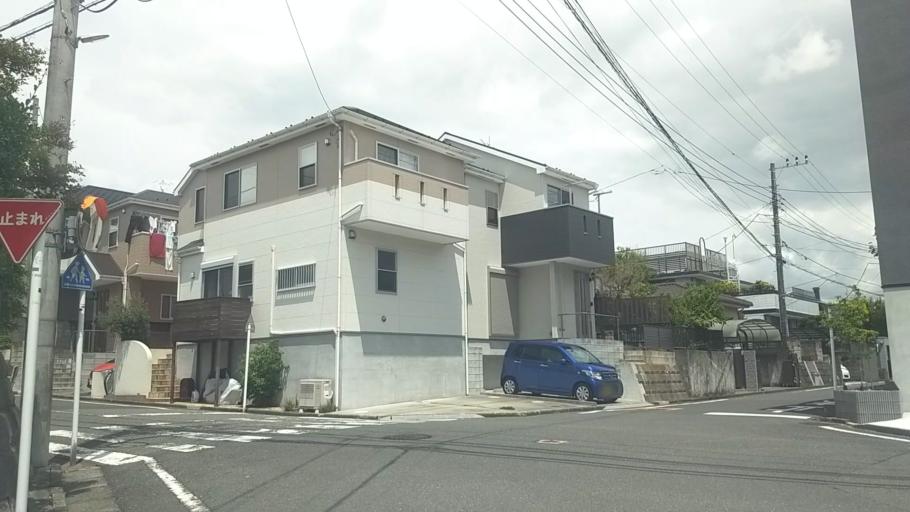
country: JP
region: Kanagawa
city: Fujisawa
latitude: 35.3487
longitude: 139.5023
